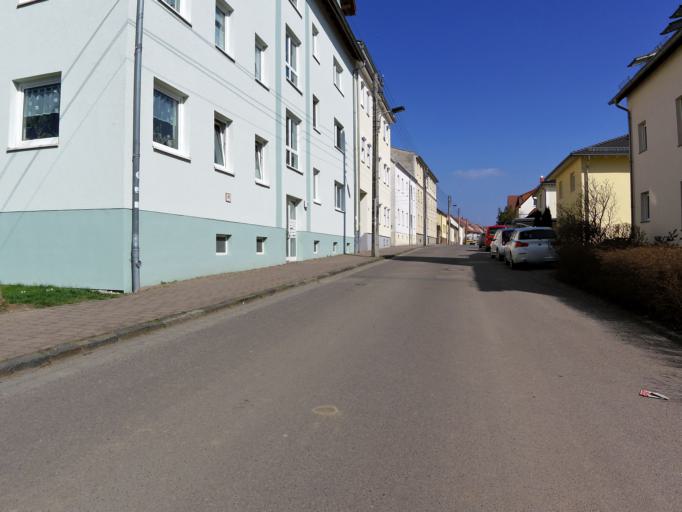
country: DE
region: Saxony
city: Schkeuditz
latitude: 51.3779
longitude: 12.2997
